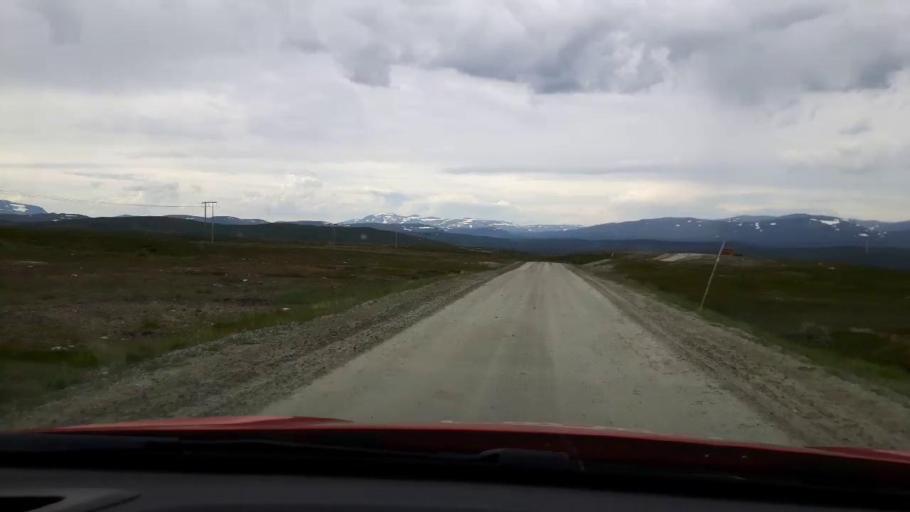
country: SE
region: Jaemtland
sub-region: Are Kommun
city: Are
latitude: 62.7668
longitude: 12.7664
